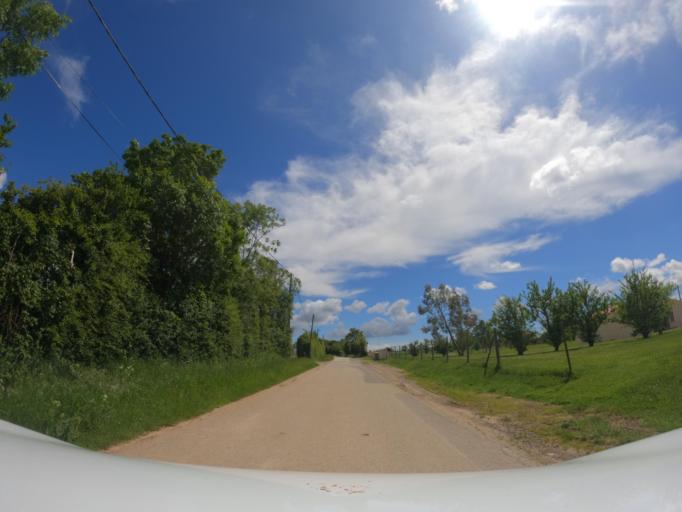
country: FR
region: Pays de la Loire
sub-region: Departement de la Vendee
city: Le Champ-Saint-Pere
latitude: 46.4891
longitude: -1.3218
